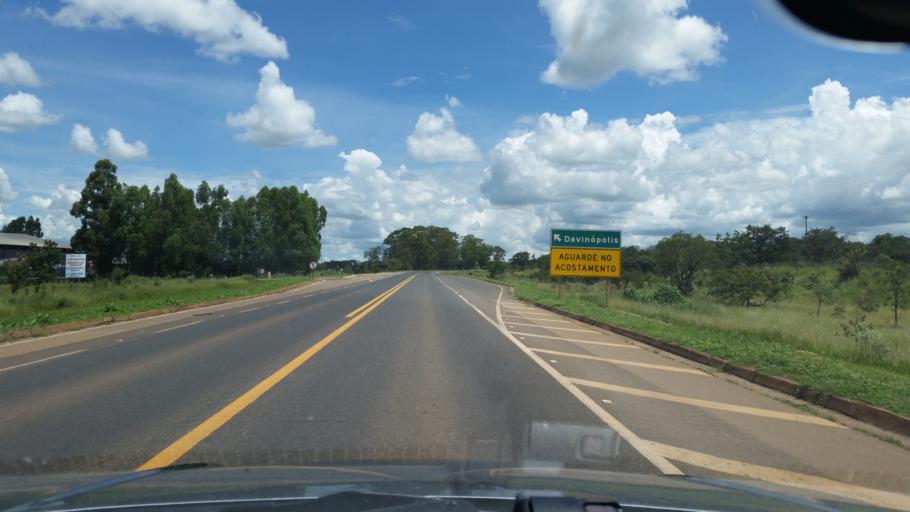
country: BR
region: Goias
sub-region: Catalao
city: Catalao
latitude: -18.0695
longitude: -47.8643
